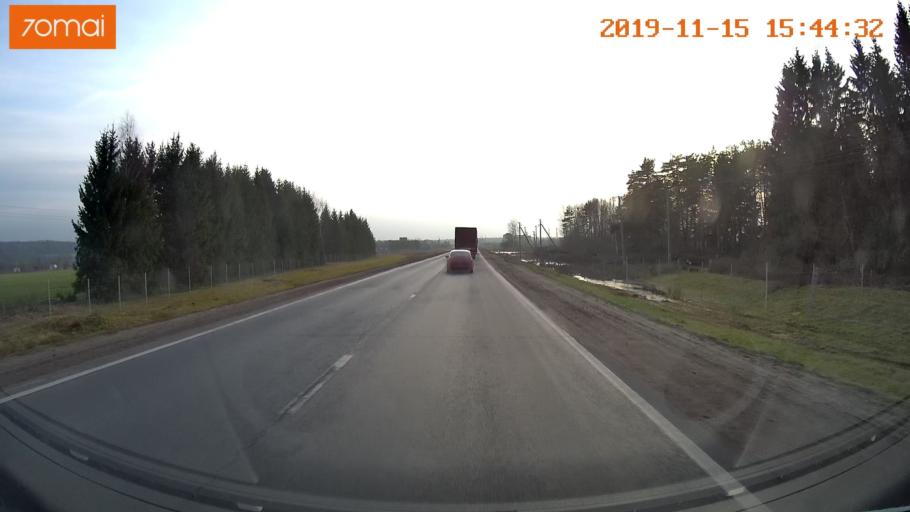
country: RU
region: Jaroslavl
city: Danilov
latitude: 57.9693
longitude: 40.0212
